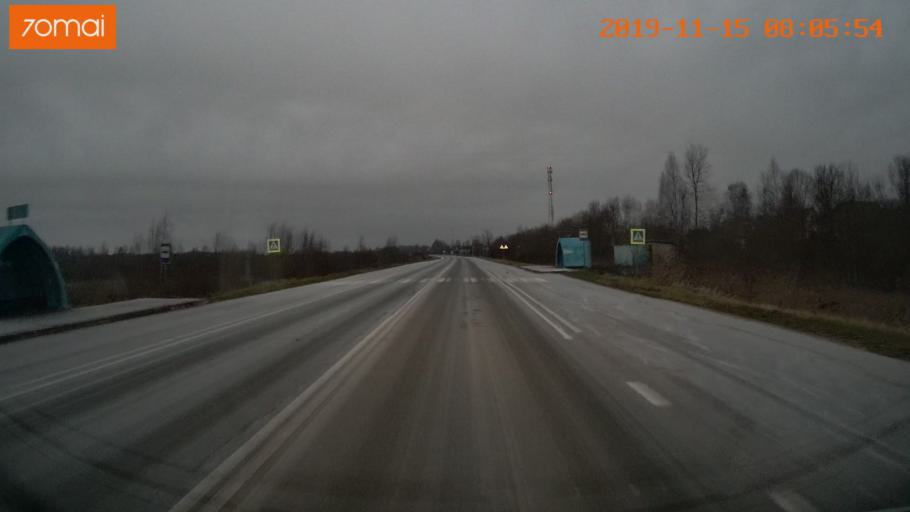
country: RU
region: Vologda
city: Cherepovets
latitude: 59.0194
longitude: 38.0487
